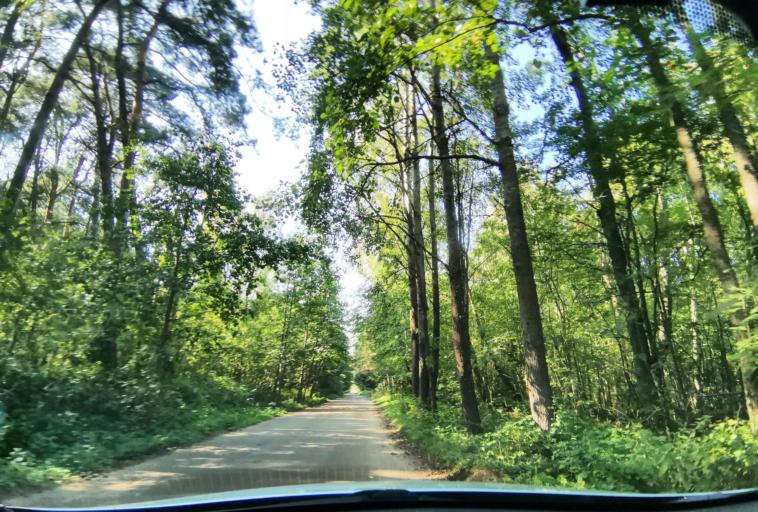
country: LT
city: Nida
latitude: 55.1624
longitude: 20.8236
